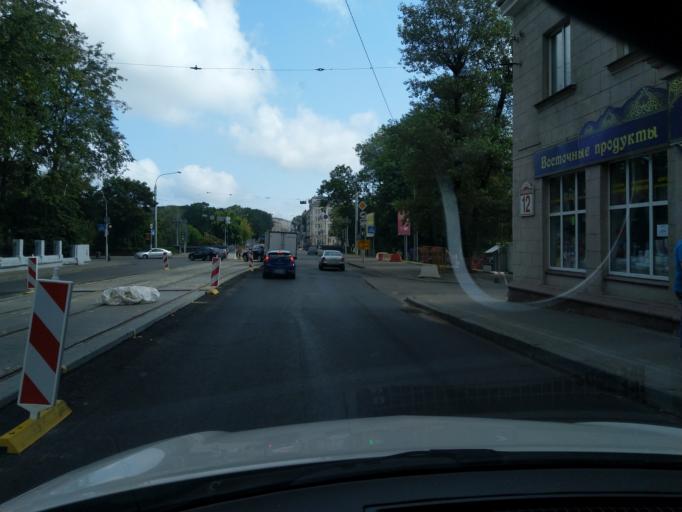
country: BY
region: Minsk
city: Minsk
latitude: 53.8989
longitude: 27.5712
